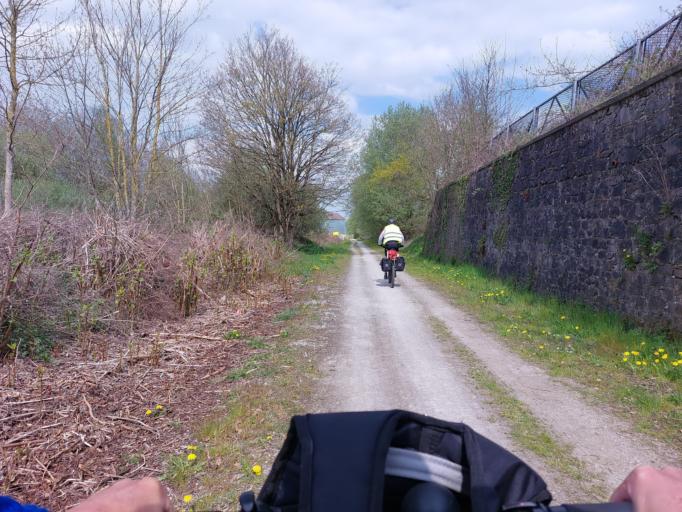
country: FR
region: Nord-Pas-de-Calais
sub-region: Departement du Nord
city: Hautmont
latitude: 50.2473
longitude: 3.9042
